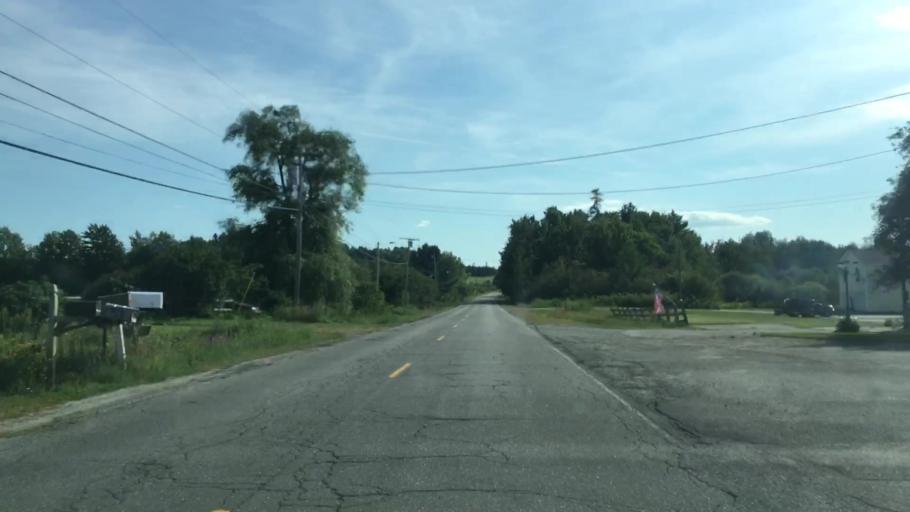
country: US
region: Maine
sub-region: Penobscot County
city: Lincoln
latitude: 45.3249
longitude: -68.5324
